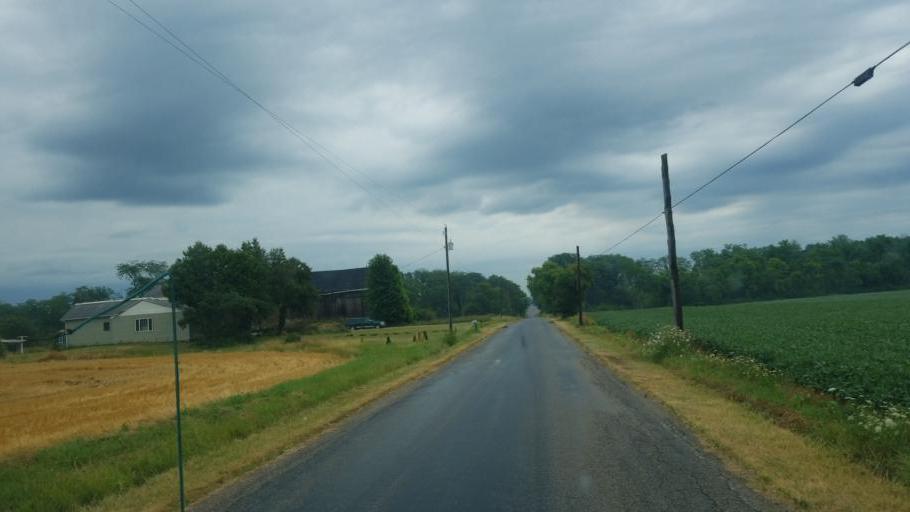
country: US
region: Indiana
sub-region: DeKalb County
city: Butler
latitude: 41.4432
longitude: -84.8859
